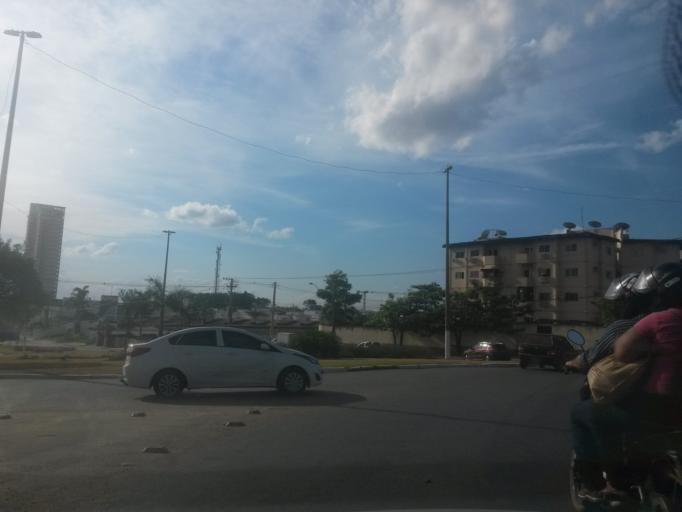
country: BR
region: Mato Grosso
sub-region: Cuiaba
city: Cuiaba
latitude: -15.5649
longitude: -56.0861
